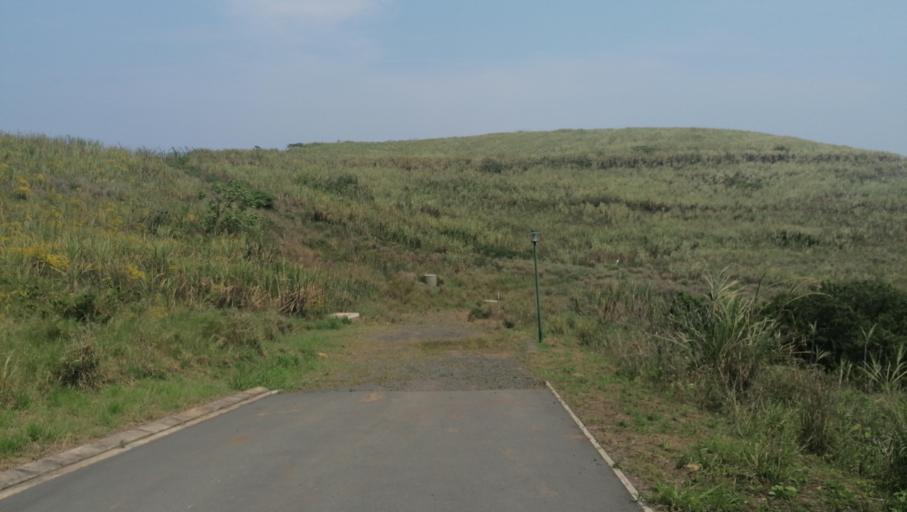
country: ZA
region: KwaZulu-Natal
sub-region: iLembe District Municipality
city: Stanger
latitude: -29.4313
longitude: 31.2670
